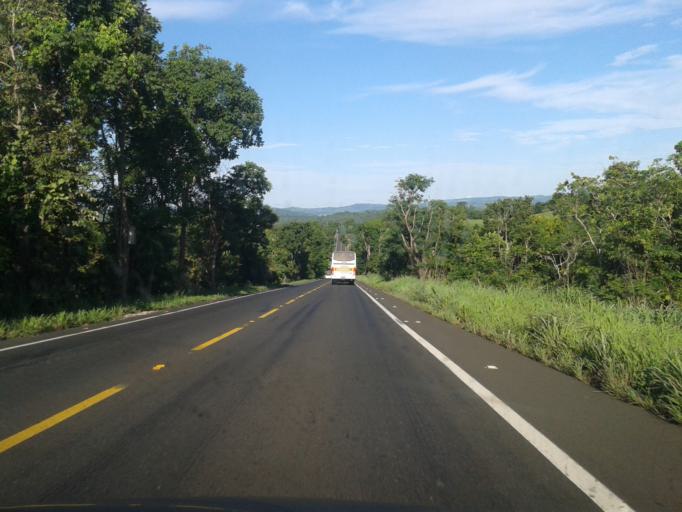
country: BR
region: Goias
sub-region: Caldas Novas
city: Caldas Novas
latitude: -18.1158
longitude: -48.6046
